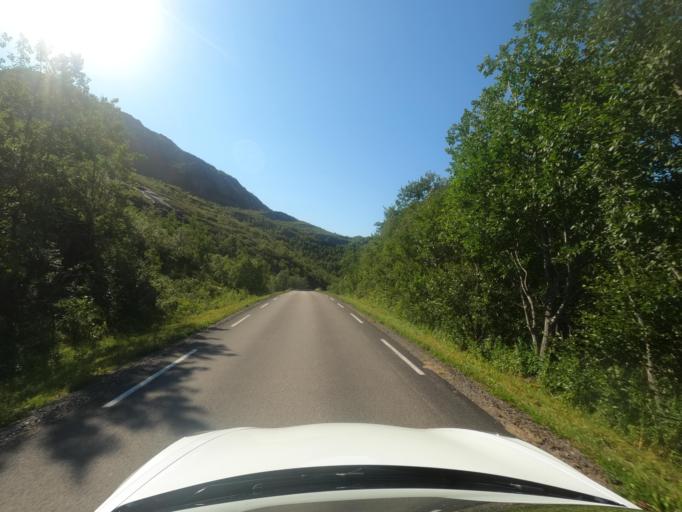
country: NO
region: Nordland
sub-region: Hadsel
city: Stokmarknes
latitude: 68.3296
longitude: 15.0156
